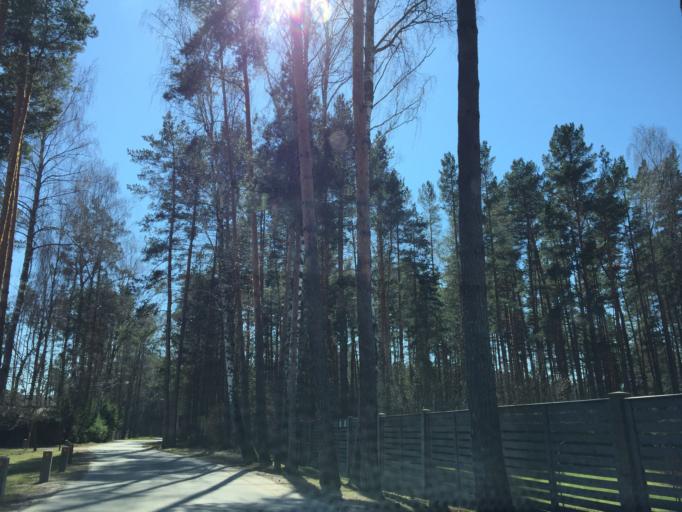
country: LV
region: Jurmala
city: Jurmala
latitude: 56.9463
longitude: 23.6841
